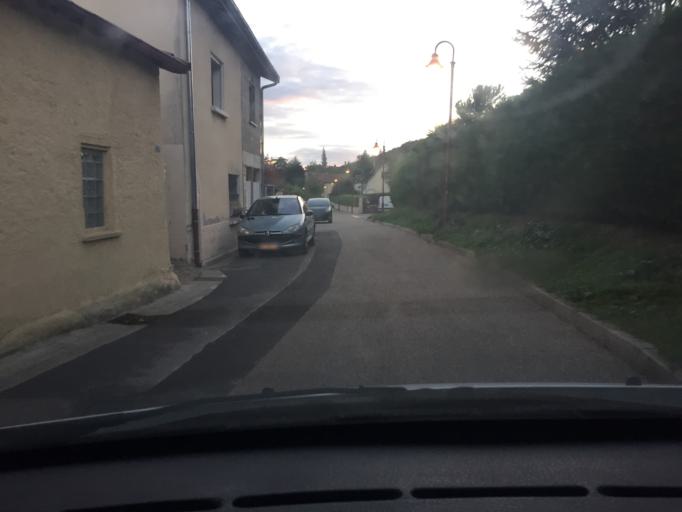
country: FR
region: Rhone-Alpes
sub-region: Departement de l'Ain
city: Saint-Maurice-de-Beynost
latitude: 45.8367
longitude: 4.9835
